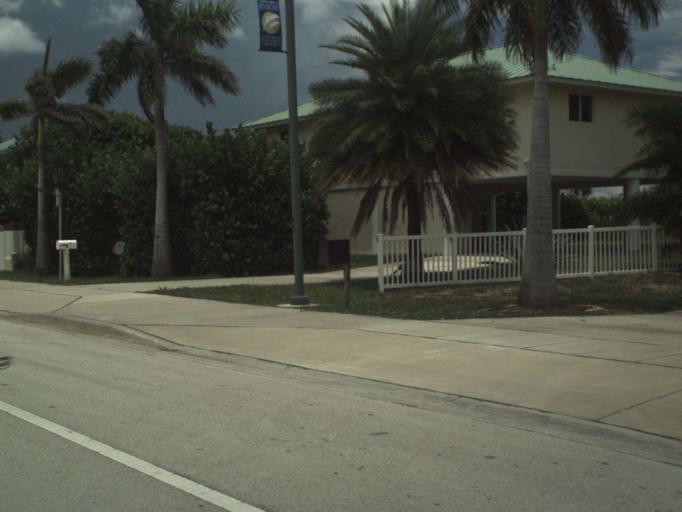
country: US
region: Florida
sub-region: Saint Lucie County
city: Fort Pierce
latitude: 27.4566
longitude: -80.2872
